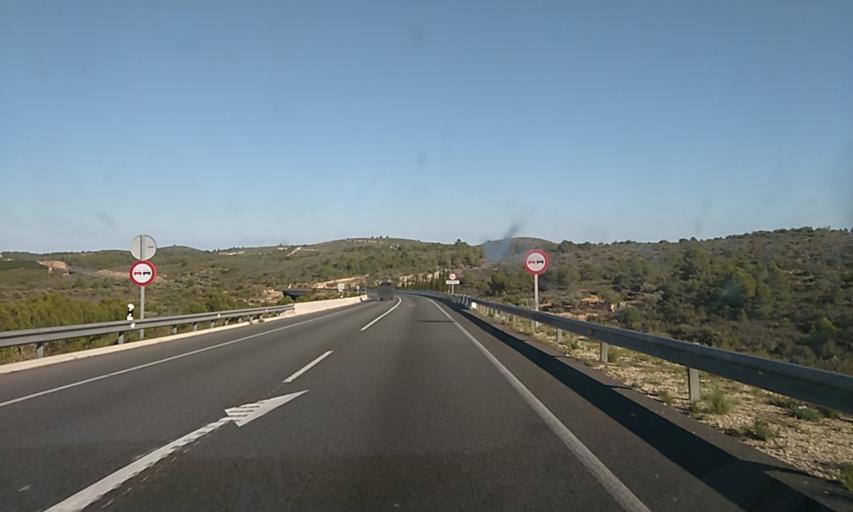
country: ES
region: Valencia
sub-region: Provincia de Castello
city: Torreblanca
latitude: 40.2103
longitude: 0.1349
